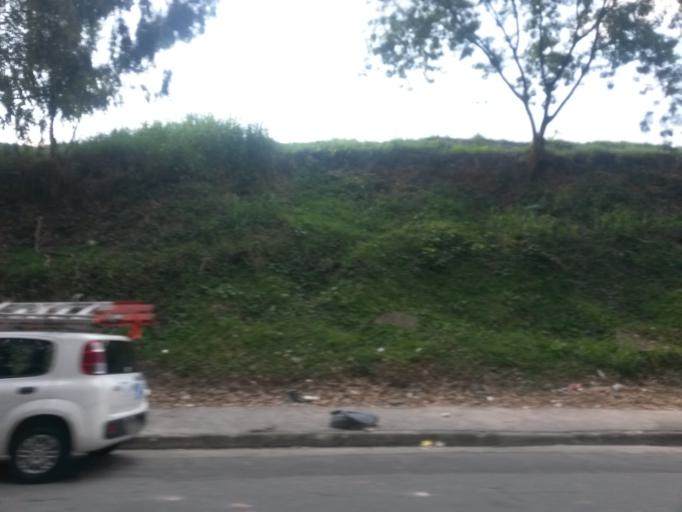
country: BR
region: Sao Paulo
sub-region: Sao Bernardo Do Campo
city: Sao Bernardo do Campo
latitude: -23.7076
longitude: -46.5725
